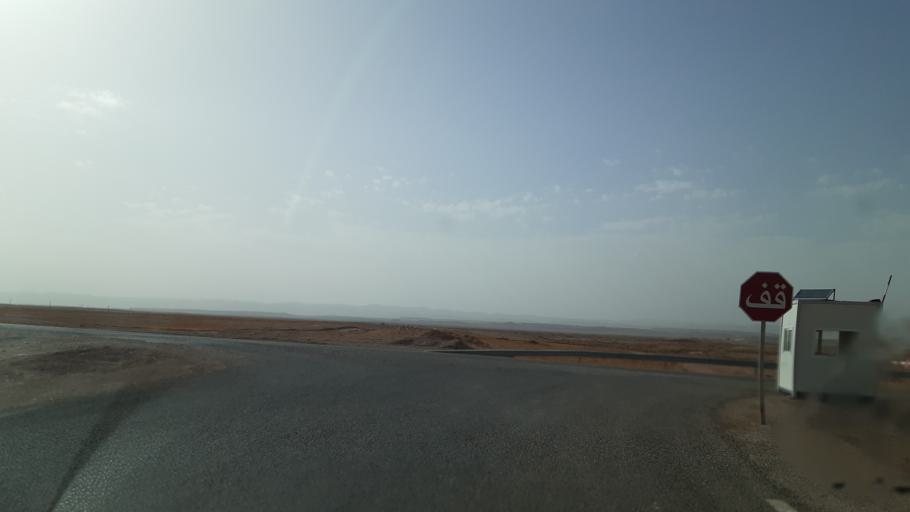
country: MA
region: Meknes-Tafilalet
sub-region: Khenifra
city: Midelt
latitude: 32.8832
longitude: -4.7101
